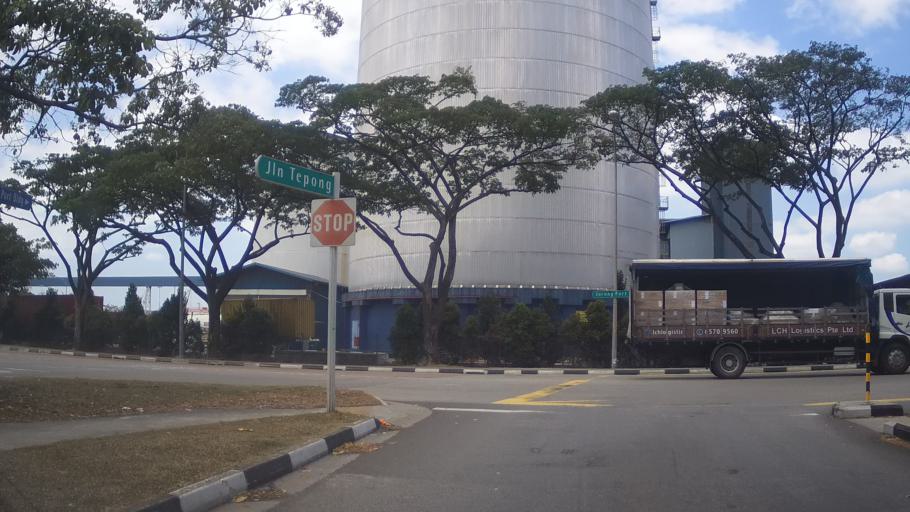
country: SG
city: Singapore
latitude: 1.3115
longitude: 103.7192
